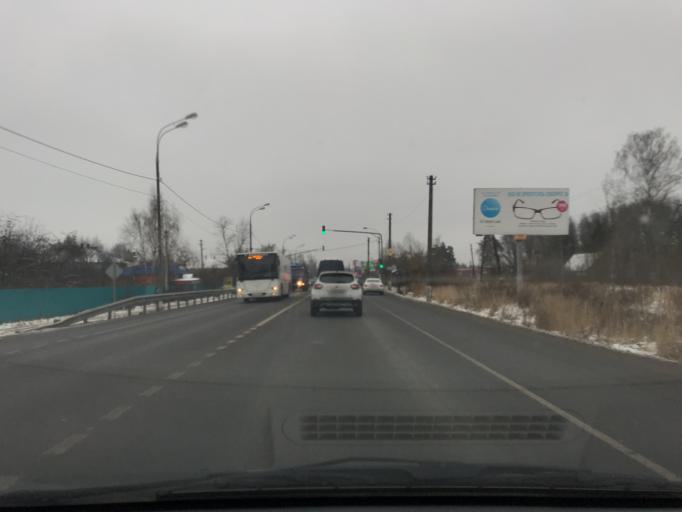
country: RU
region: Moskovskaya
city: Elektrostal'
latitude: 55.8089
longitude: 38.4271
